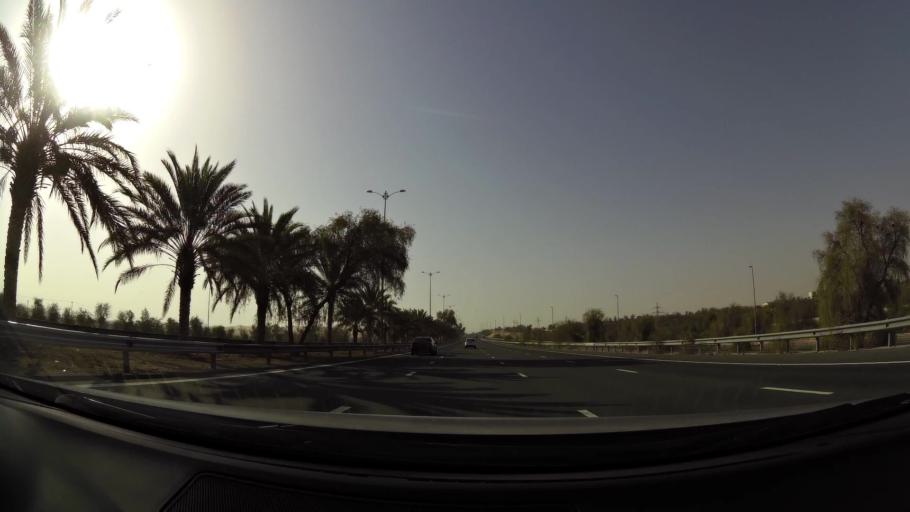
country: OM
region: Al Buraimi
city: Al Buraymi
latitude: 24.6400
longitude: 55.7113
